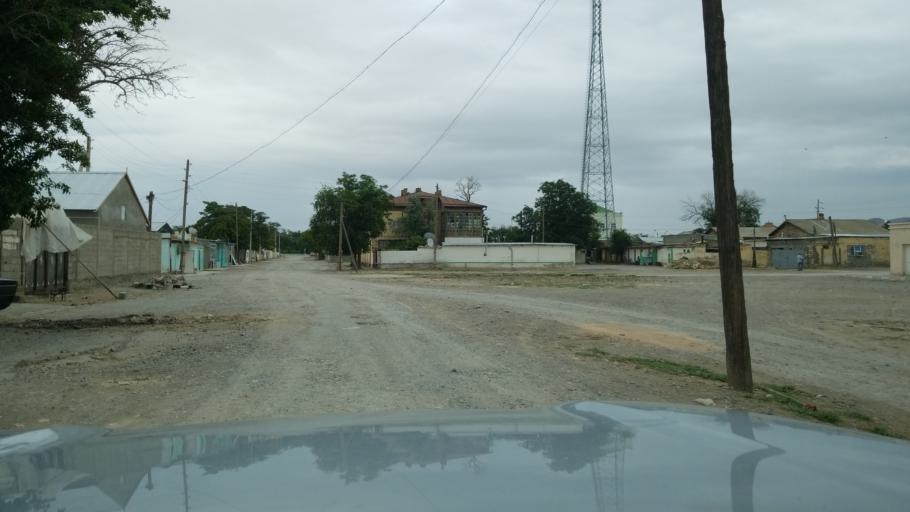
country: TM
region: Balkan
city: Serdar
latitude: 38.9804
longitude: 56.2712
